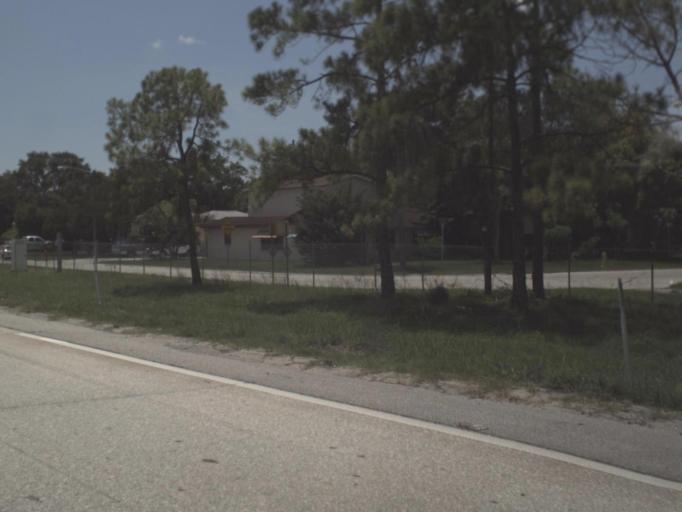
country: US
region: Florida
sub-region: Pinellas County
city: Lealman
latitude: 27.8032
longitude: -82.6629
